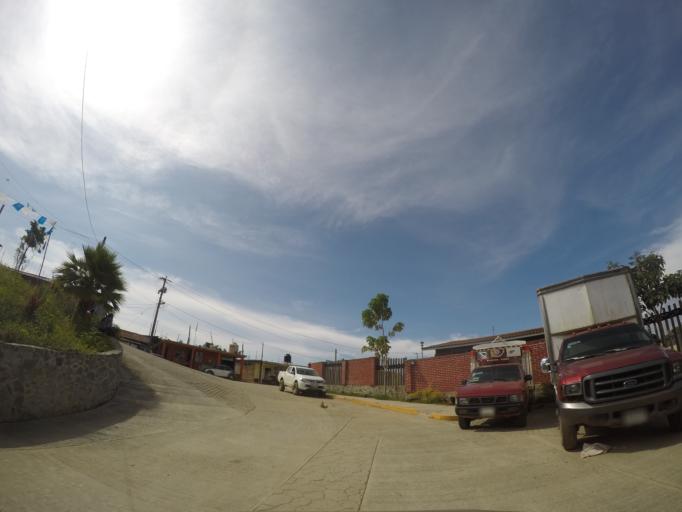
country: MX
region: Oaxaca
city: Pluma Hidalgo
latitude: 15.9293
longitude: -96.4173
